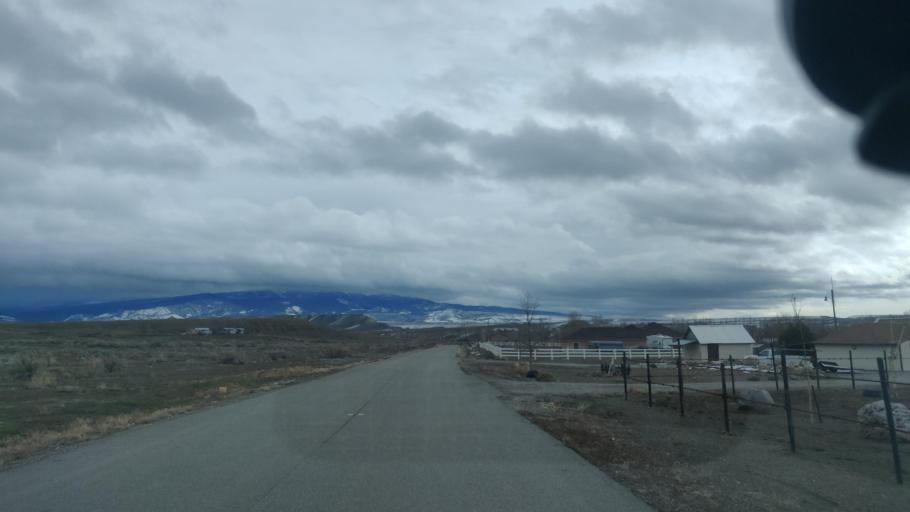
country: US
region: Colorado
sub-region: Mesa County
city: Clifton
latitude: 38.9433
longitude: -108.4024
